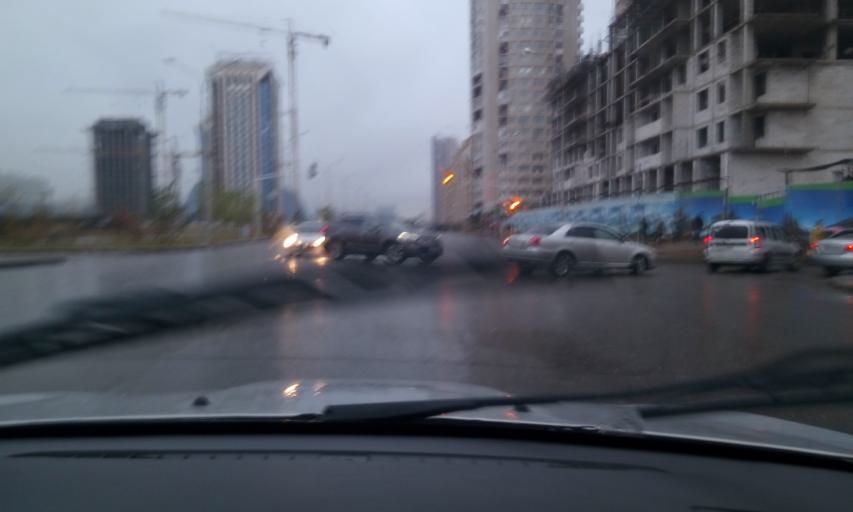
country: KZ
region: Astana Qalasy
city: Astana
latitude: 51.1227
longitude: 71.4821
